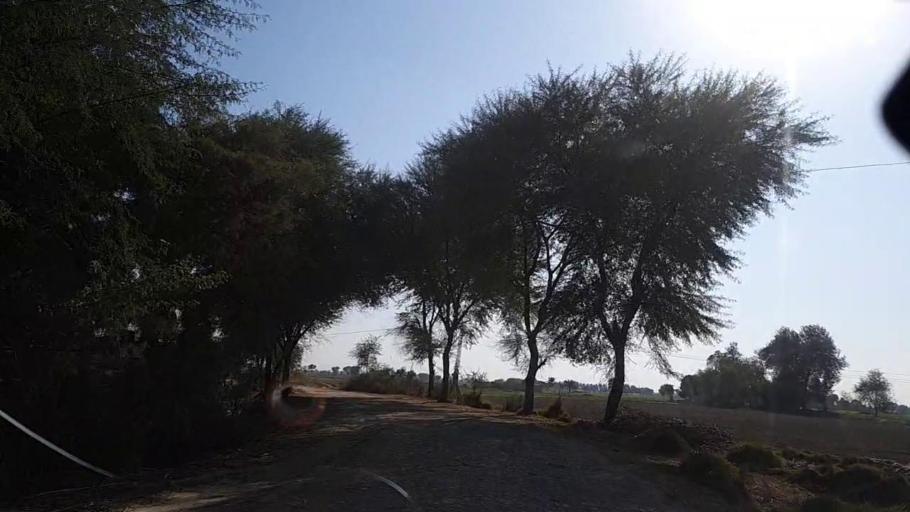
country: PK
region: Sindh
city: Khanpur
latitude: 27.8052
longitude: 69.3699
